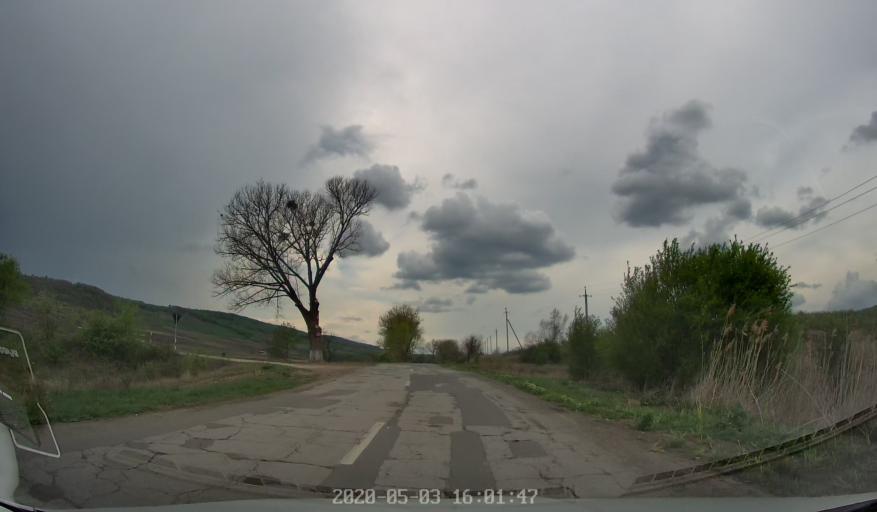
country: MD
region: Stinga Nistrului
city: Bucovat
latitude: 47.1690
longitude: 28.4047
